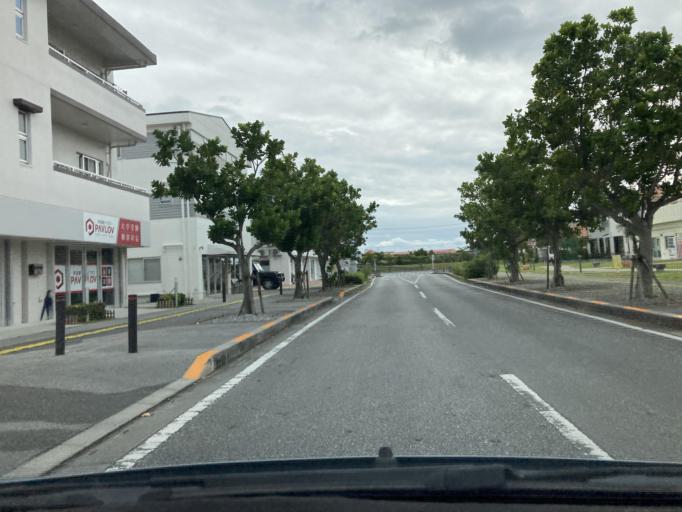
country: JP
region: Okinawa
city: Itoman
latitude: 26.1541
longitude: 127.6626
